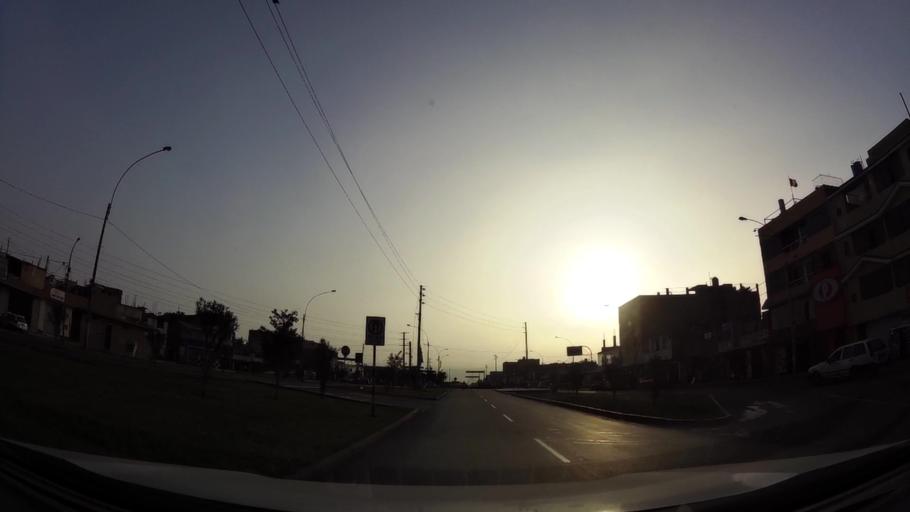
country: PE
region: Lima
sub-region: Lima
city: Independencia
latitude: -11.9904
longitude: -77.0956
